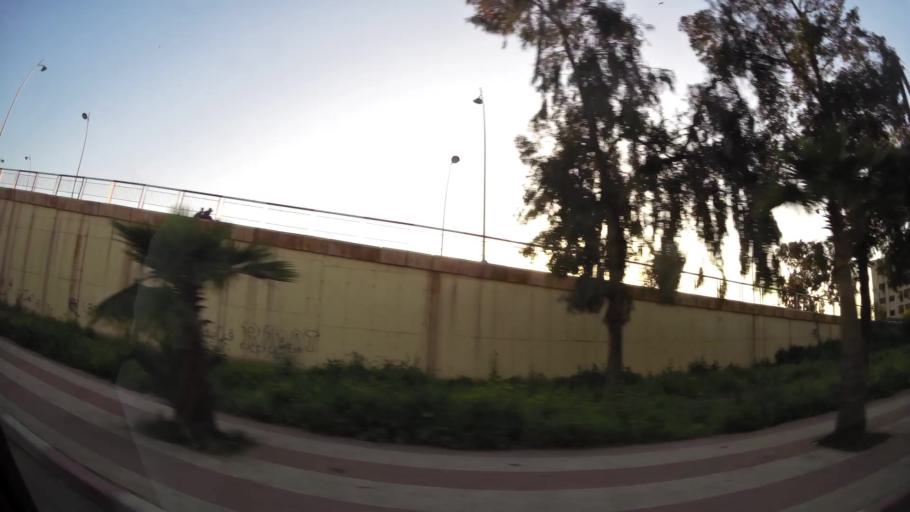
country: MA
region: Chaouia-Ouardigha
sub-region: Settat Province
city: Settat
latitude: 32.9906
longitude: -7.6208
